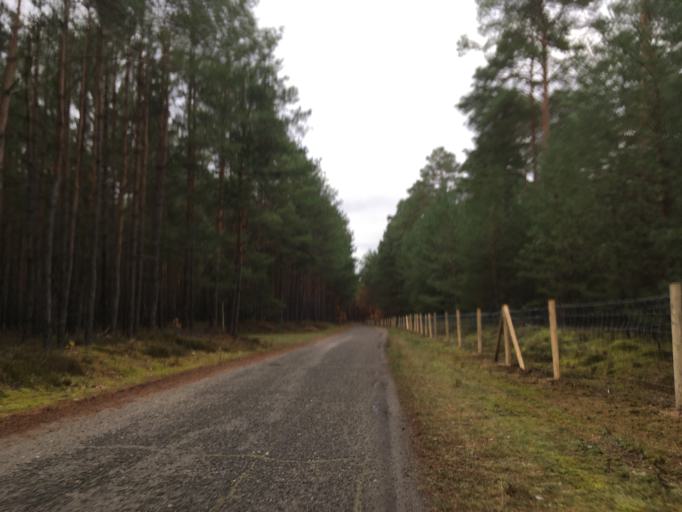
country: DE
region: Brandenburg
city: Jamlitz
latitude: 52.0616
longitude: 14.4815
